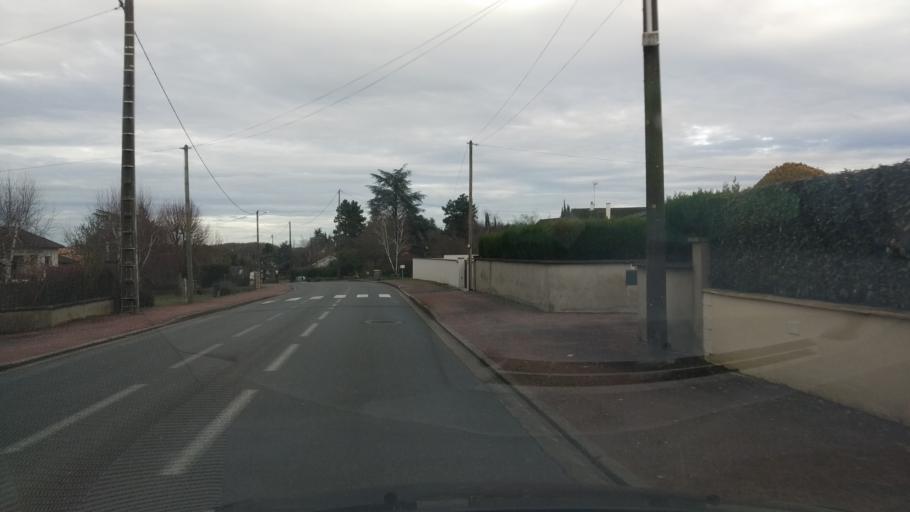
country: FR
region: Poitou-Charentes
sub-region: Departement de la Vienne
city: Dissay
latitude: 46.6902
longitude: 0.4176
